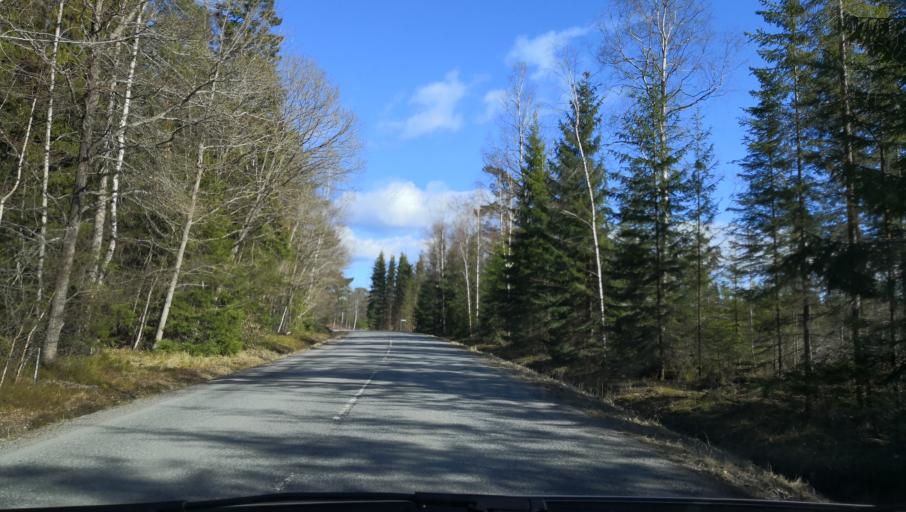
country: SE
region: Stockholm
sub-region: Varmdo Kommun
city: Holo
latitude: 59.3554
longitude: 18.5993
